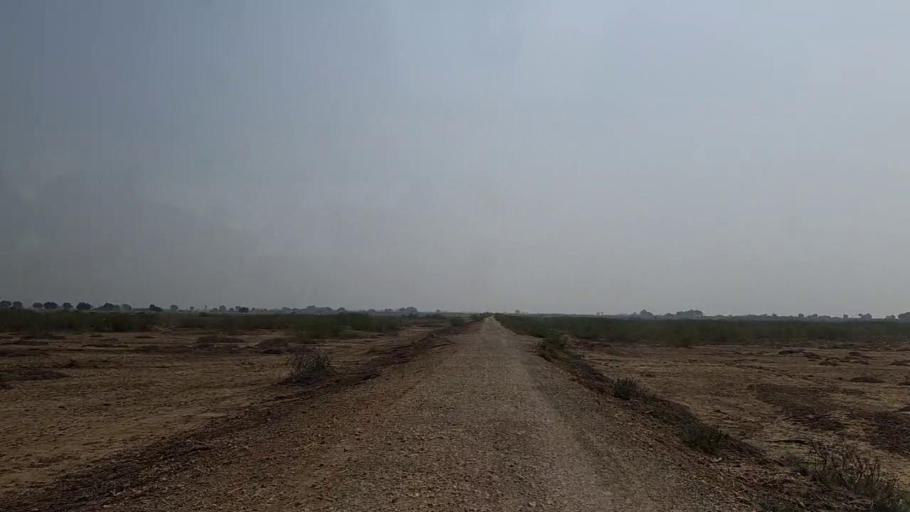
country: PK
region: Sindh
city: Naukot
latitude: 24.7925
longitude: 69.3295
